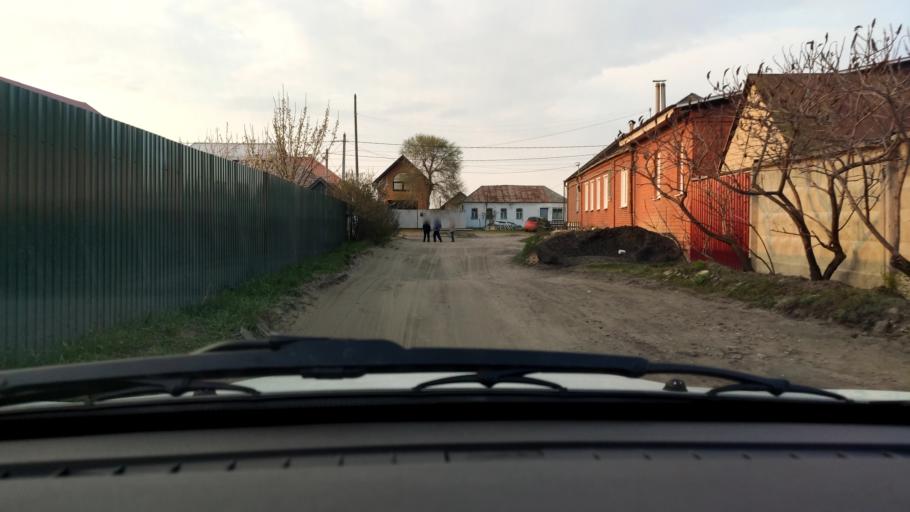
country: RU
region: Voronezj
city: Somovo
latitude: 51.7518
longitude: 39.3349
